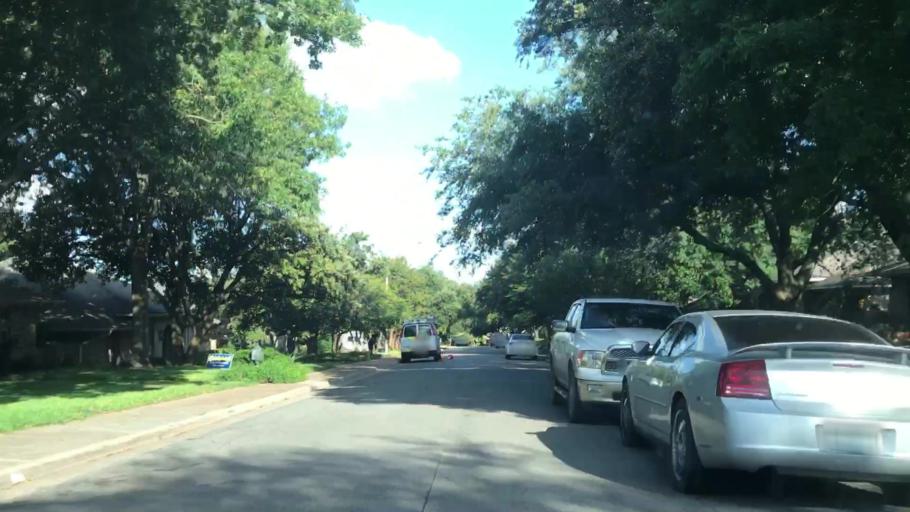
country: US
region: Texas
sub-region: Dallas County
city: Highland Park
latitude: 32.8283
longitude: -96.7507
